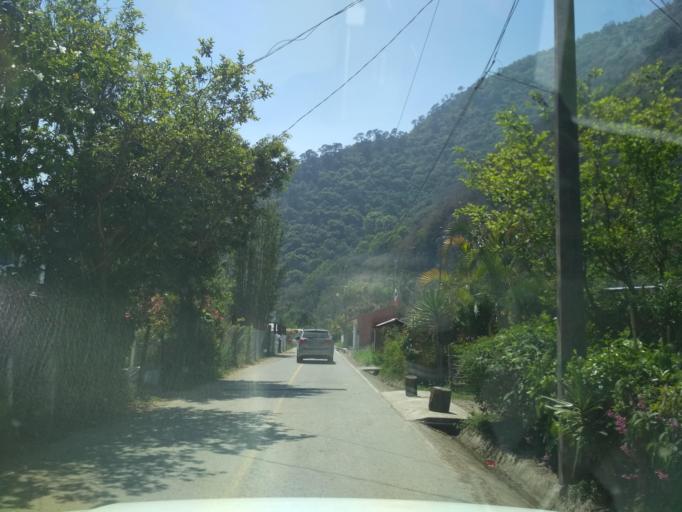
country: MX
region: Veracruz
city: Jalapilla
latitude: 18.8265
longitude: -97.1028
